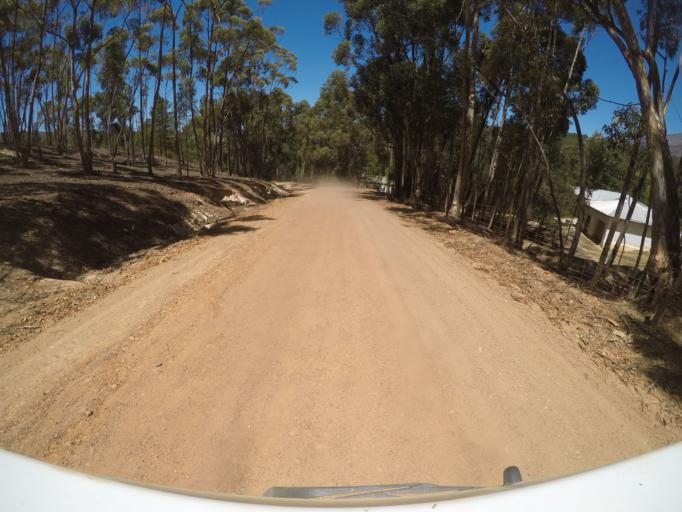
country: ZA
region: Western Cape
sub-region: Overberg District Municipality
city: Grabouw
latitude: -34.1679
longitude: 19.2247
